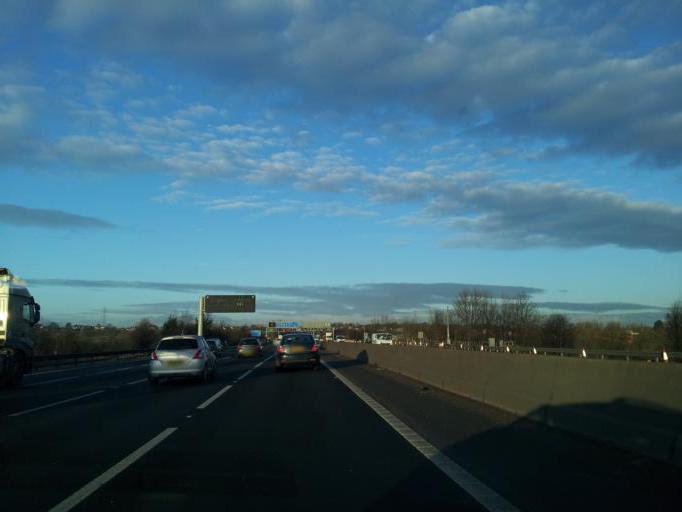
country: GB
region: England
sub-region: City and Borough of Leeds
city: Lofthouse
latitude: 53.7282
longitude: -1.4782
